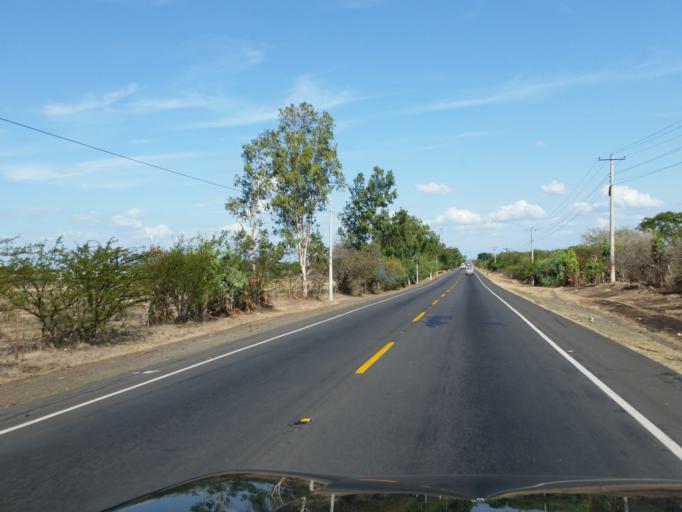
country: NI
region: Leon
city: La Paz Centro
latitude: 12.3068
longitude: -86.7794
